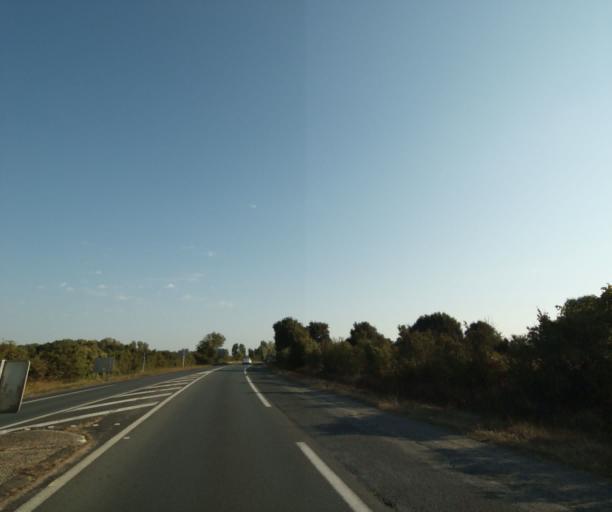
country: FR
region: Poitou-Charentes
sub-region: Departement de la Charente-Maritime
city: Saint-Hippolyte
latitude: 45.9185
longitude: -0.8860
